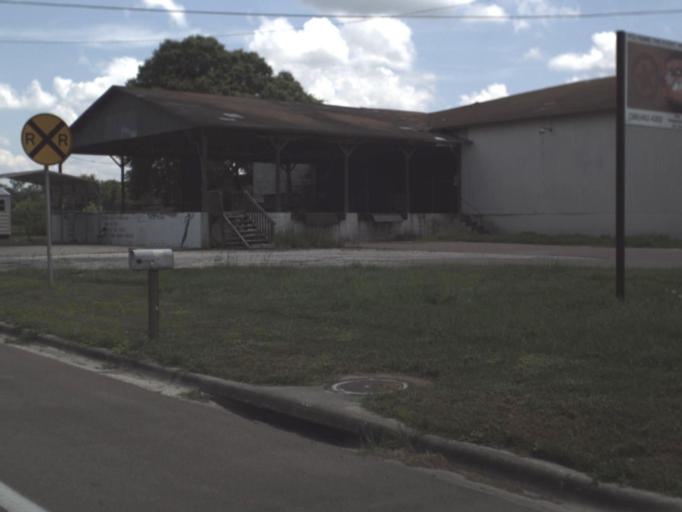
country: US
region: Florida
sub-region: Alachua County
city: Alachua
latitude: 29.8475
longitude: -82.4049
